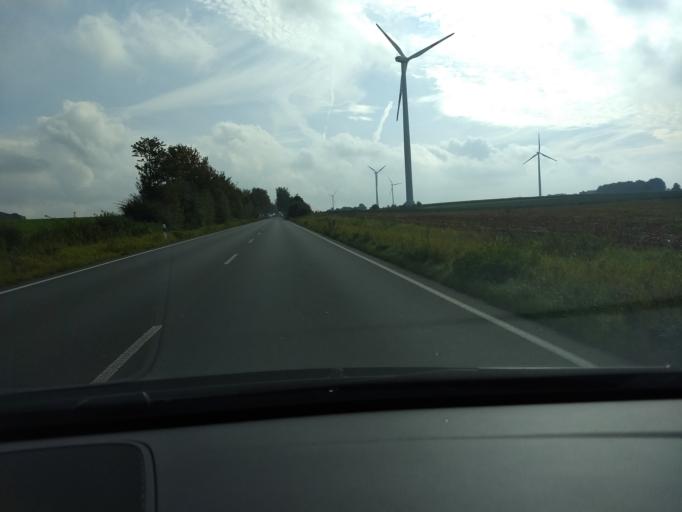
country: DE
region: North Rhine-Westphalia
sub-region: Regierungsbezirk Munster
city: Heiden
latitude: 51.8169
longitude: 6.9529
